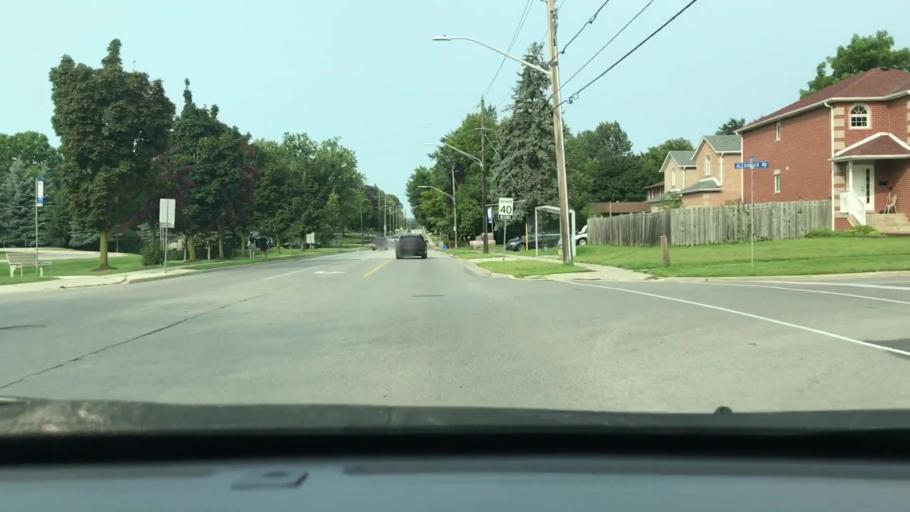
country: CA
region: Ontario
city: Newmarket
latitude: 44.0543
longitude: -79.4410
